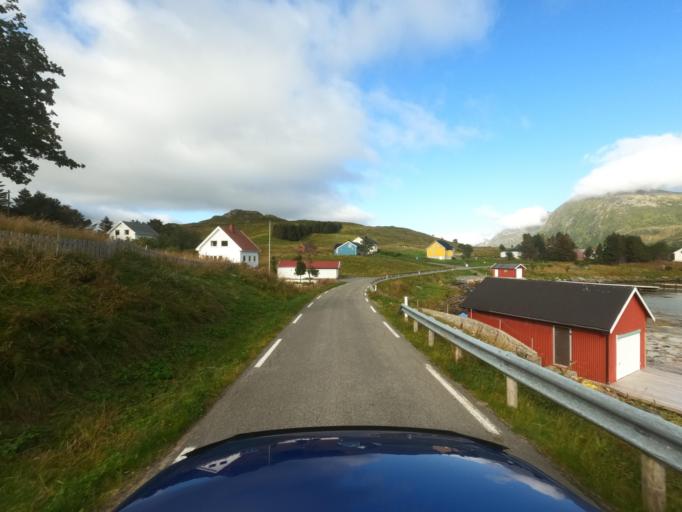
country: NO
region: Nordland
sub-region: Flakstad
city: Ramberg
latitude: 68.0571
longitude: 13.1537
